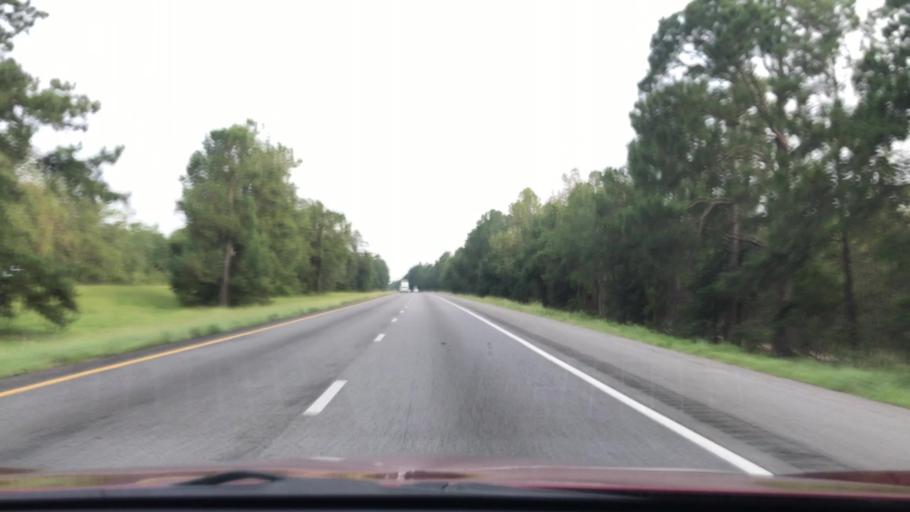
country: US
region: South Carolina
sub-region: Dorchester County
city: Ridgeville
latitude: 33.1699
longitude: -80.3640
